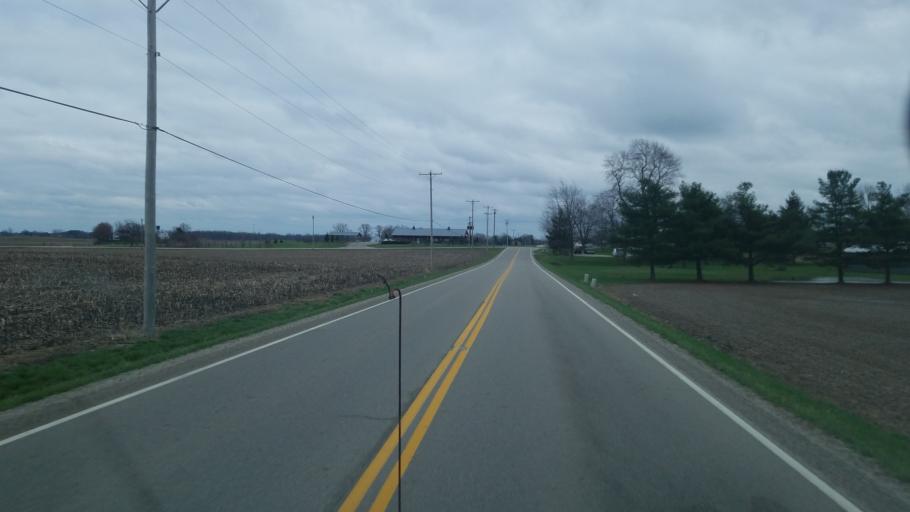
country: US
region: Ohio
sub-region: Fayette County
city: Washington Court House
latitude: 39.5494
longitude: -83.4820
